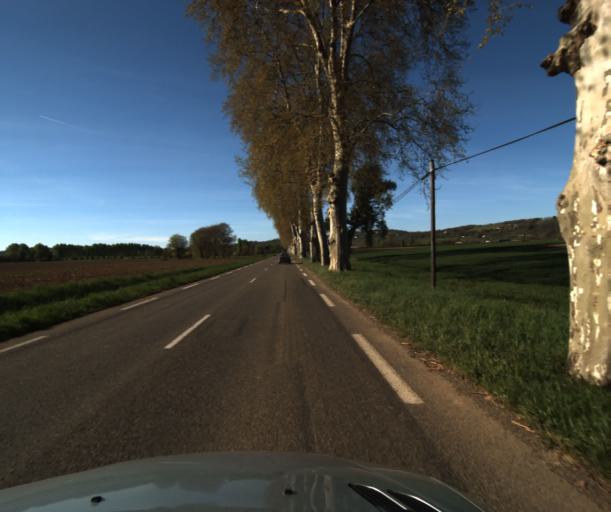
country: FR
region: Midi-Pyrenees
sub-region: Departement du Tarn-et-Garonne
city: Lafrancaise
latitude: 44.1005
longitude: 1.2569
